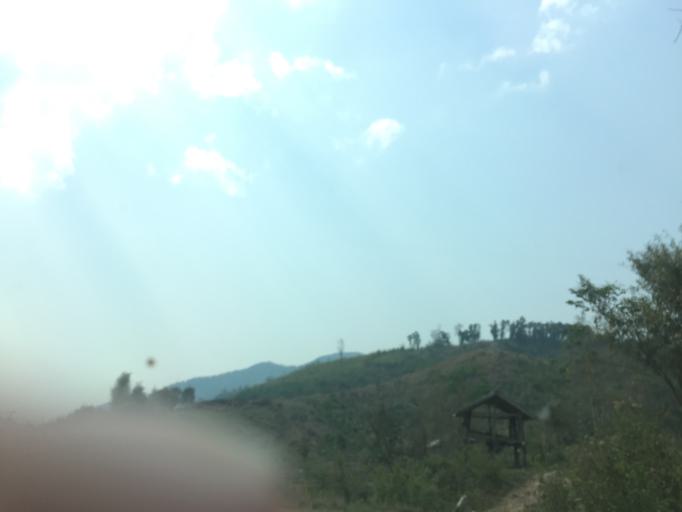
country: TH
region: Nan
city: Song Khwae
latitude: 19.7392
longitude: 100.7163
